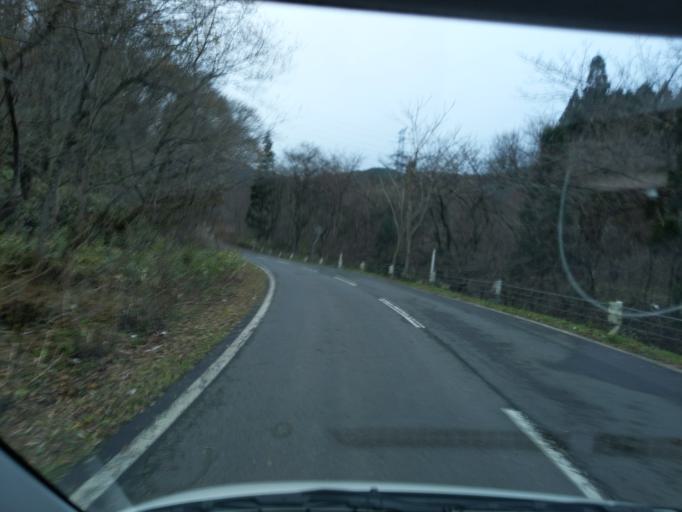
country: JP
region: Iwate
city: Tono
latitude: 39.1583
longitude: 141.3648
